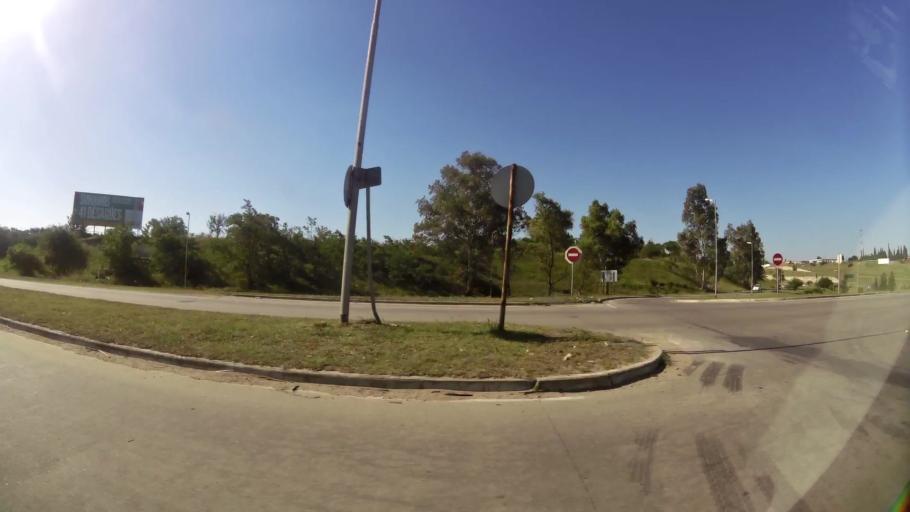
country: AR
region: Cordoba
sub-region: Departamento de Capital
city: Cordoba
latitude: -31.3978
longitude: -64.1300
